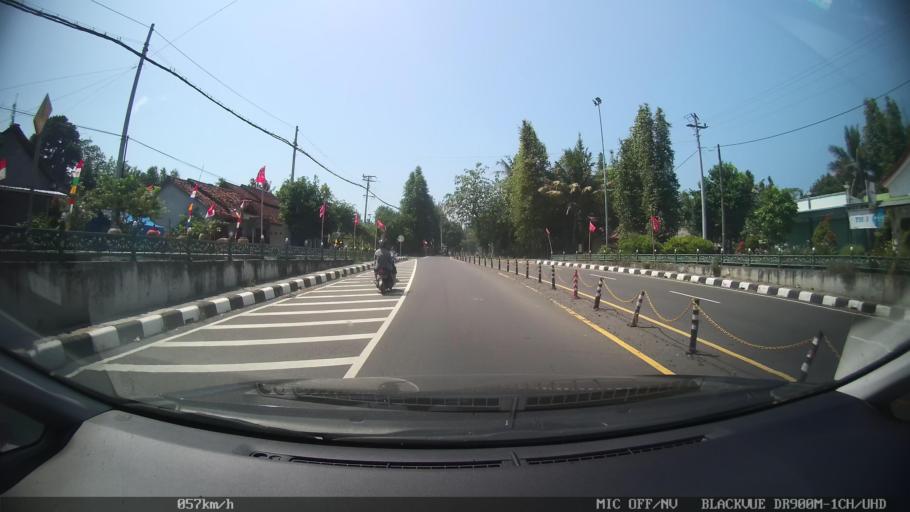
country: ID
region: Daerah Istimewa Yogyakarta
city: Srandakan
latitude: -7.8995
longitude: 110.0656
